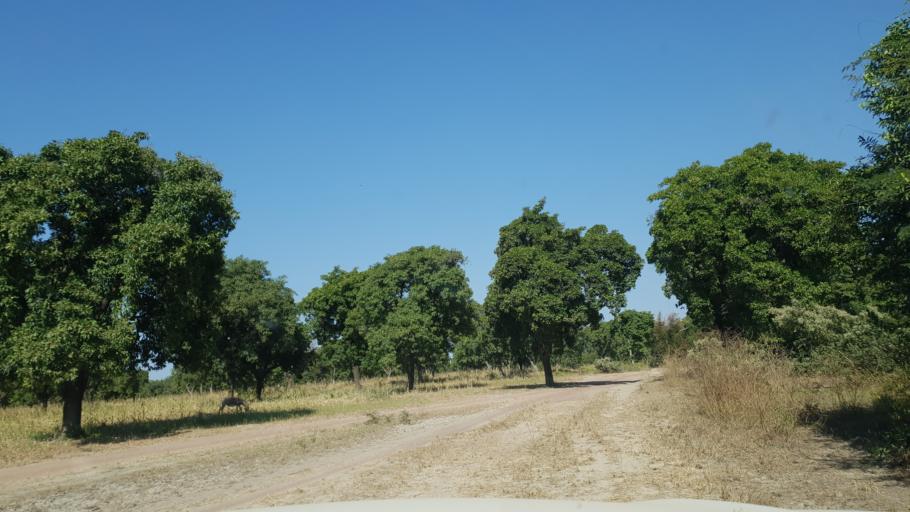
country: ML
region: Sikasso
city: Yorosso
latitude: 12.2698
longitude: -4.6970
